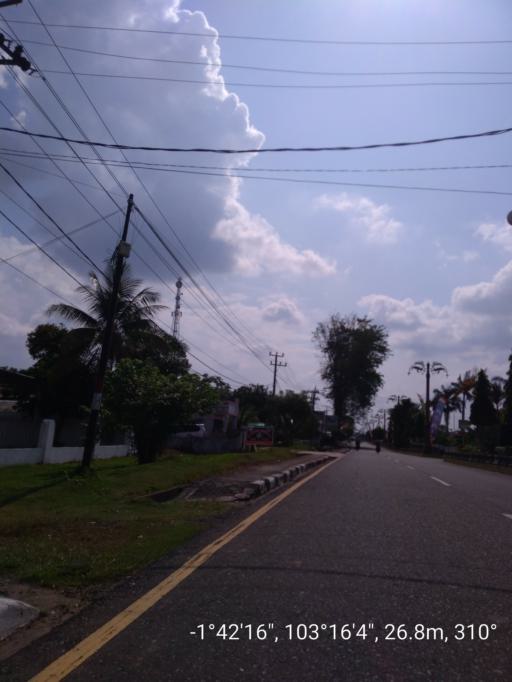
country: ID
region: Jambi
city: Muara Bulian
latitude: -1.7048
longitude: 103.2681
